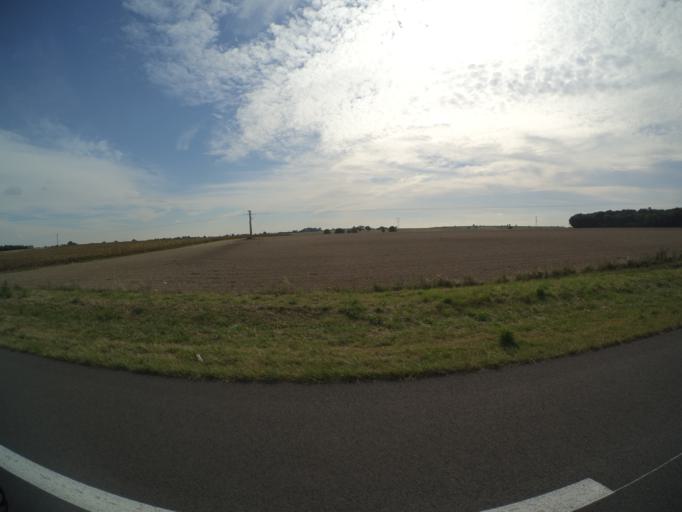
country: FR
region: Pays de la Loire
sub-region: Departement de Maine-et-Loire
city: Vaudelnay
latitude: 47.2086
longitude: -0.1886
